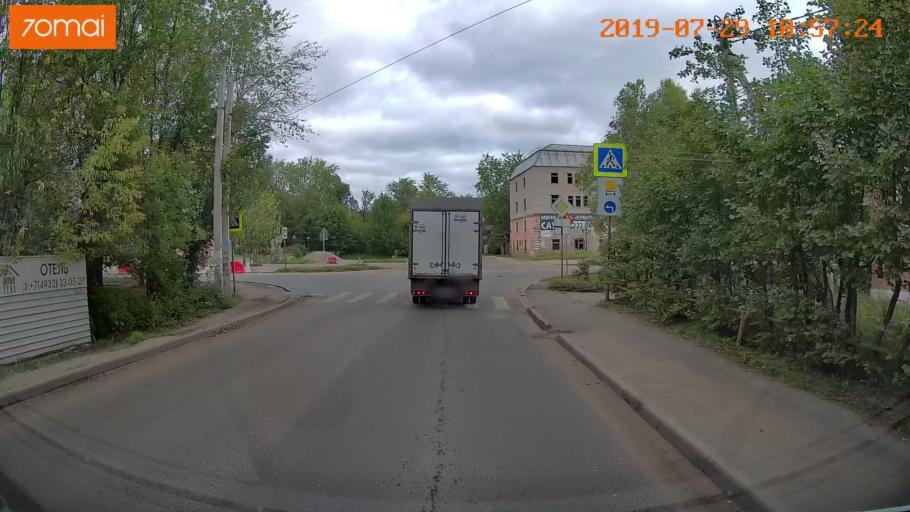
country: RU
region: Ivanovo
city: Bogorodskoye
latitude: 56.9889
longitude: 41.0366
